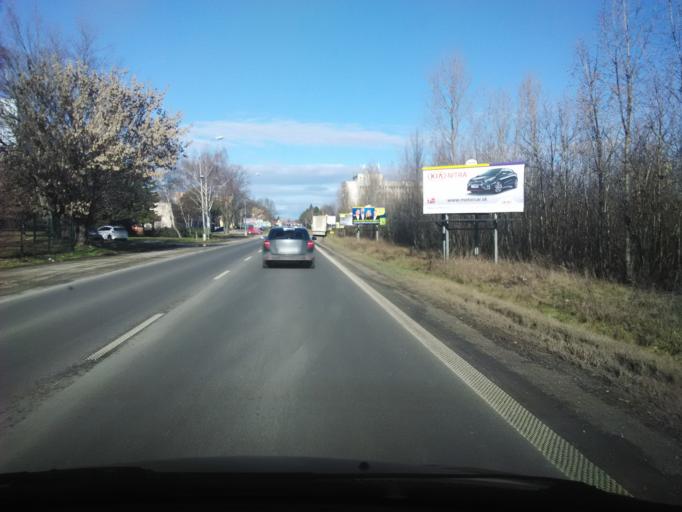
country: SK
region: Nitriansky
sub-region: Okres Nitra
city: Nitra
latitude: 48.2654
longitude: 18.1032
